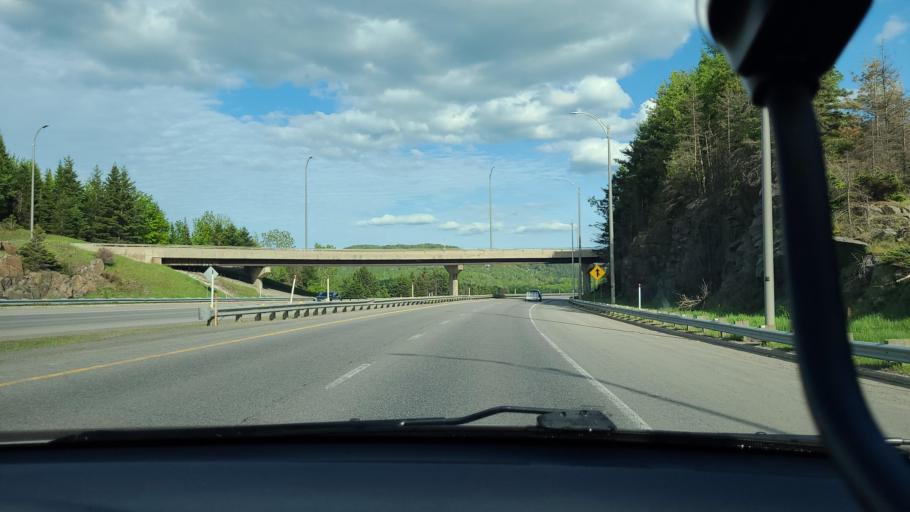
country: CA
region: Quebec
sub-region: Laurentides
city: Sainte-Adele
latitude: 45.9594
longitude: -74.1337
